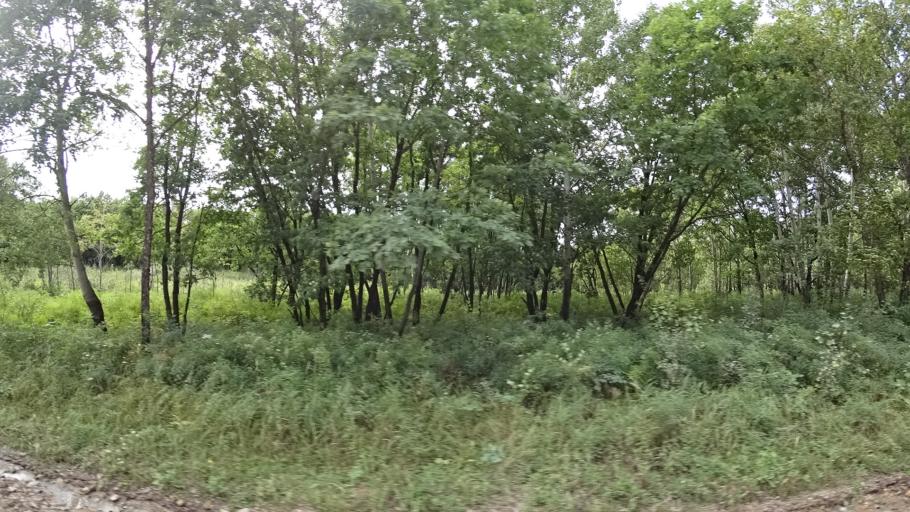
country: RU
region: Primorskiy
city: Lyalichi
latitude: 44.0902
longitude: 132.4344
